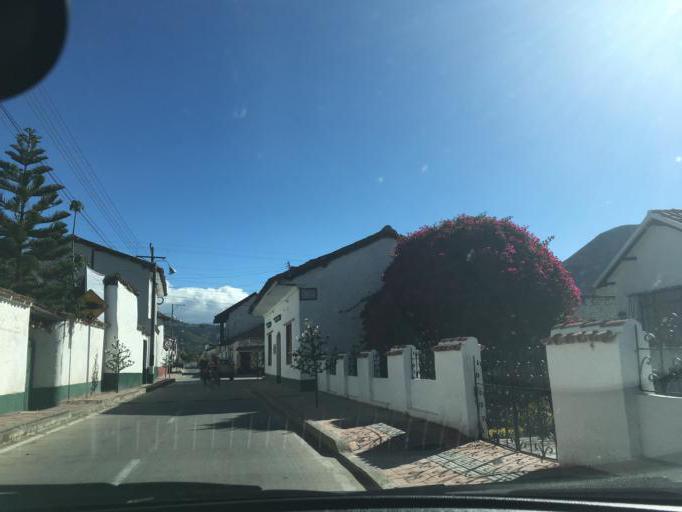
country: CO
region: Boyaca
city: Firavitoba
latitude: 5.6135
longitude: -72.9802
